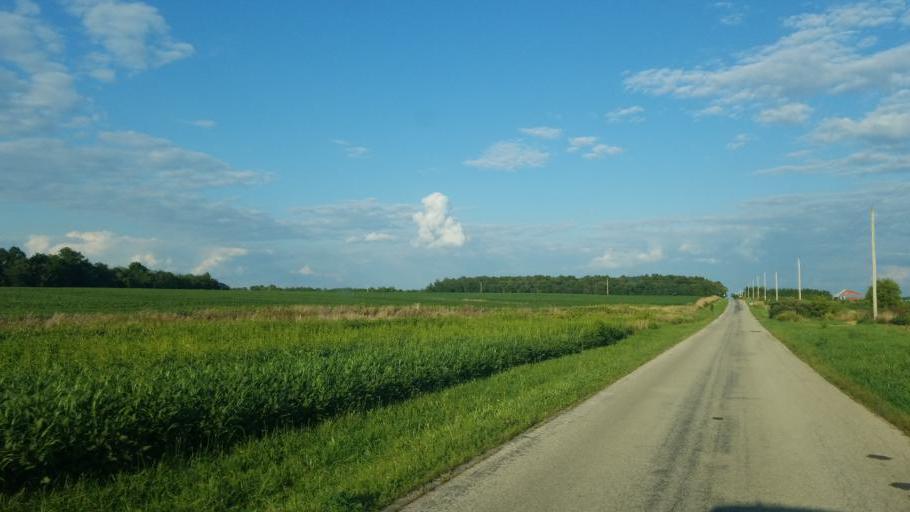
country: US
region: Ohio
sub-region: Huron County
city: Willard
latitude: 41.1098
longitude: -82.8469
